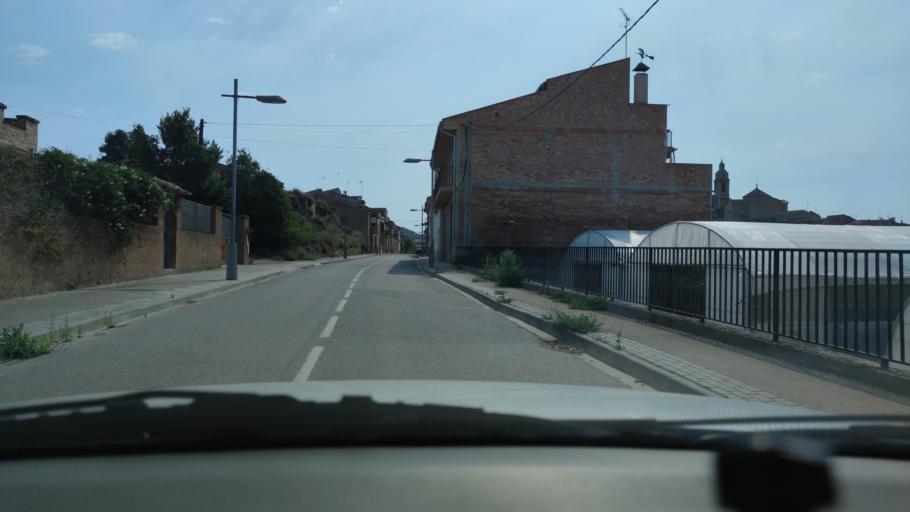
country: ES
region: Catalonia
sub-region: Provincia de Lleida
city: Fulleda
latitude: 41.4960
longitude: 1.0001
